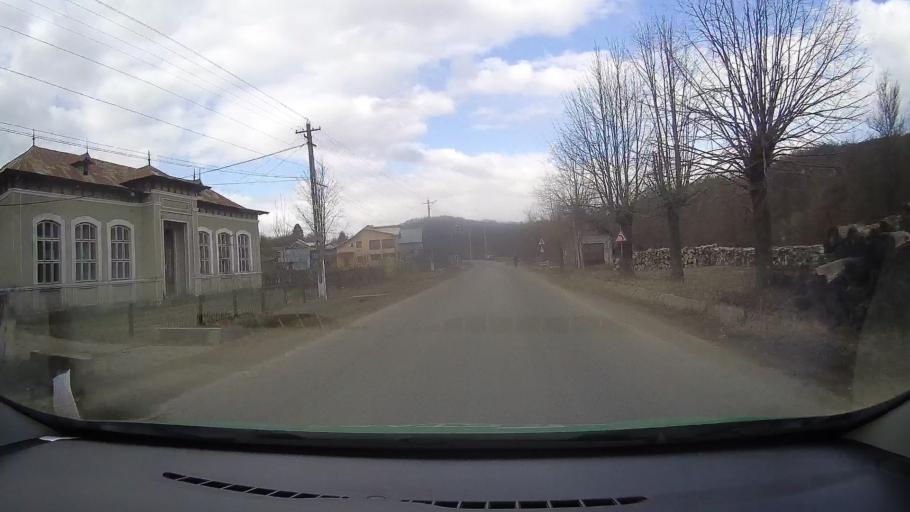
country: RO
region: Dambovita
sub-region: Comuna Valea Lunga
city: Valea Lunga-Cricov
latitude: 45.0648
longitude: 25.5573
